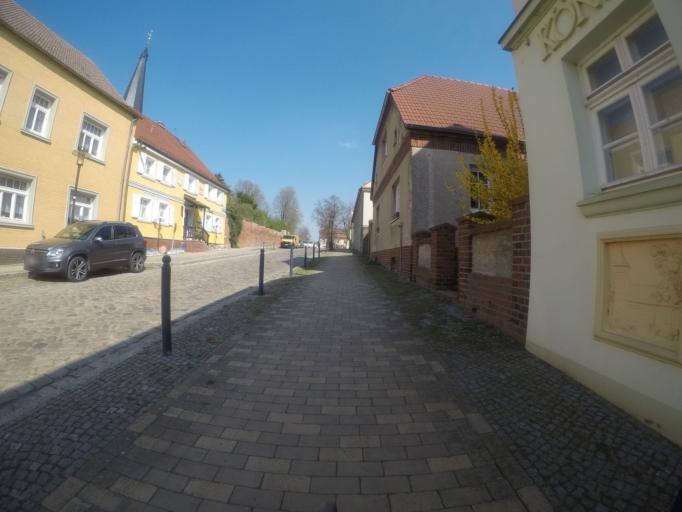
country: DE
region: Brandenburg
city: Ketzin
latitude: 52.4752
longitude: 12.8407
